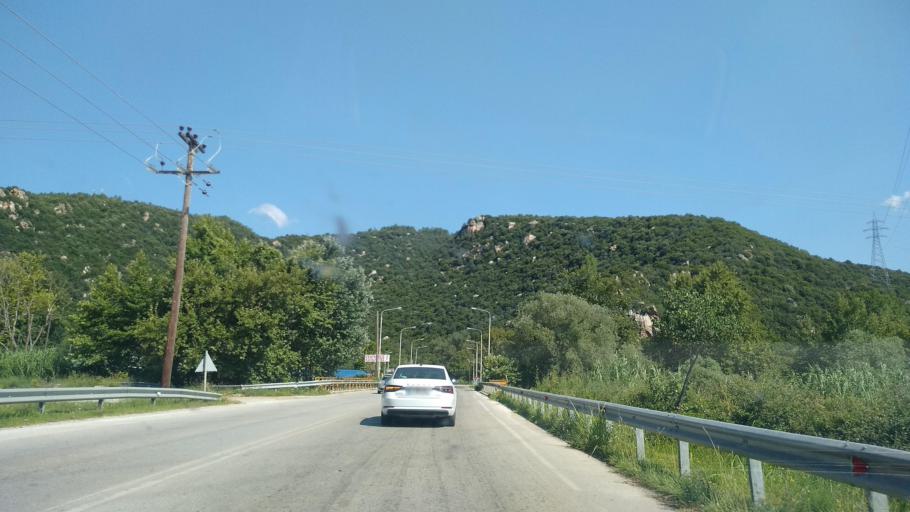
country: GR
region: Central Macedonia
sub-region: Nomos Thessalonikis
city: Stavros
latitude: 40.6718
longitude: 23.6641
